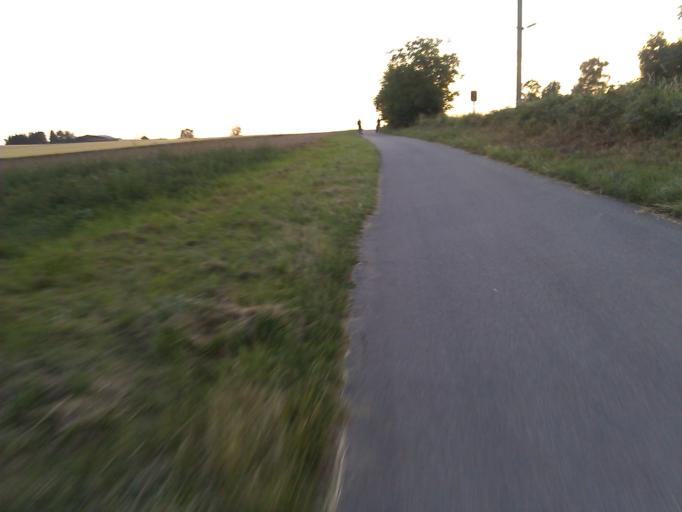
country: DE
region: Baden-Wuerttemberg
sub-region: Regierungsbezirk Stuttgart
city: Nordheim
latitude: 49.1393
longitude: 9.1644
